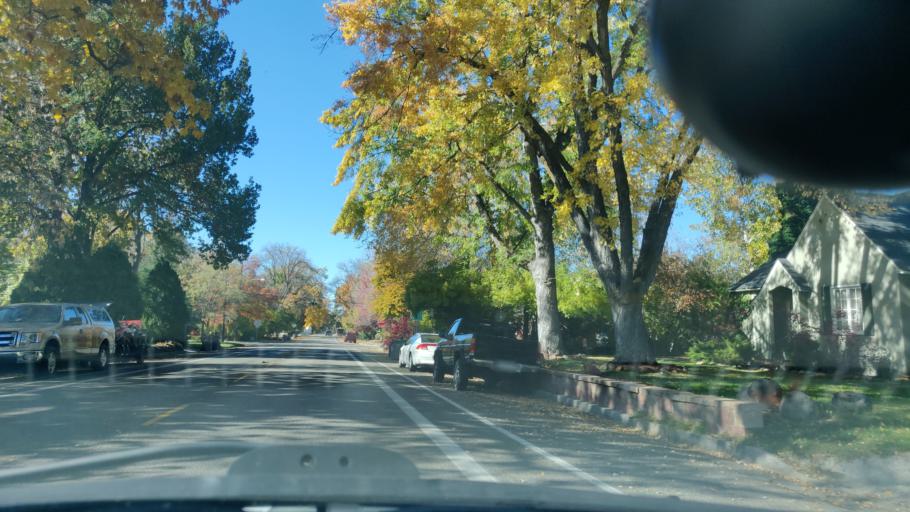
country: US
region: Idaho
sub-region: Ada County
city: Boise
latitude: 43.5935
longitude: -116.2176
